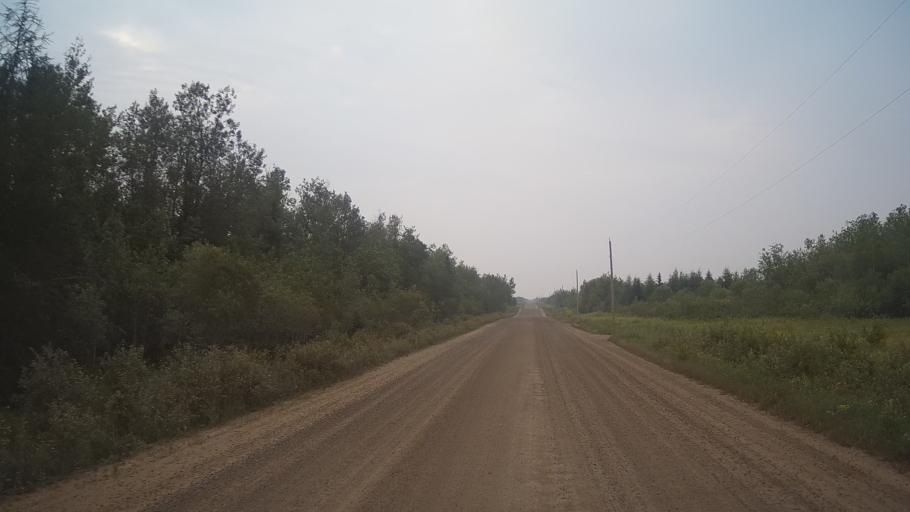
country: CA
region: Ontario
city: Hearst
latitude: 49.6372
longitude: -83.2783
